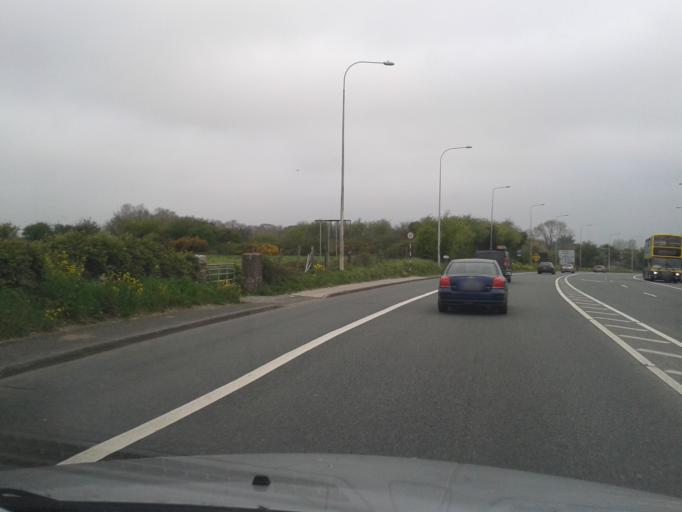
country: IE
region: Leinster
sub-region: Fingal County
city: Swords
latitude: 53.4468
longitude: -6.2283
